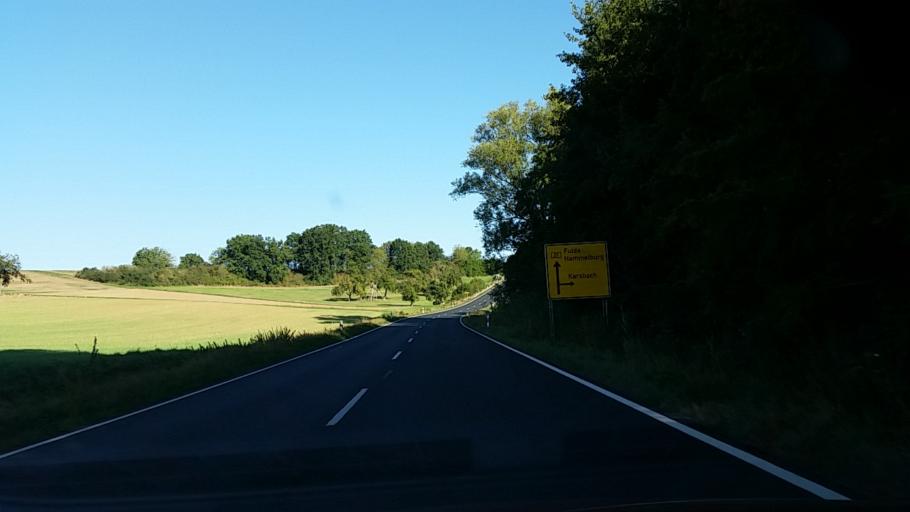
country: DE
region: Bavaria
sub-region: Regierungsbezirk Unterfranken
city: Karsbach
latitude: 50.0356
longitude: 9.7805
